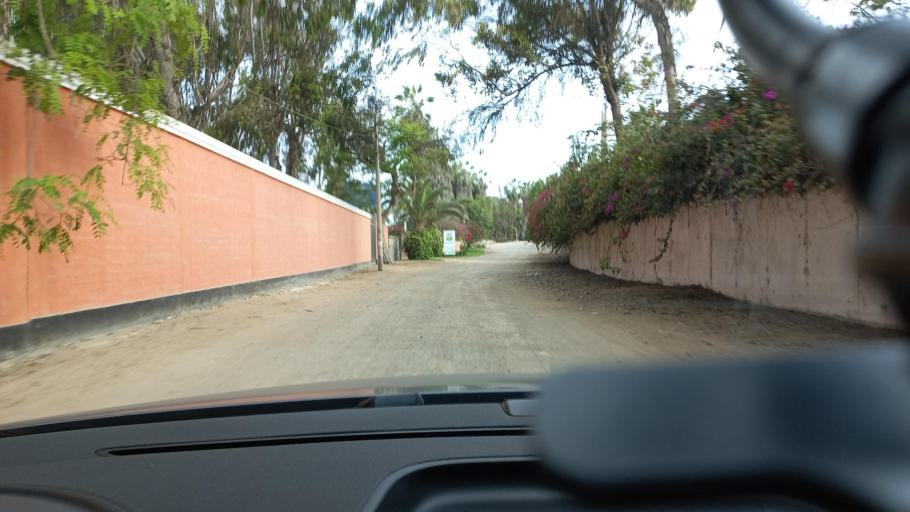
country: PE
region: Lima
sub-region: Lima
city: Punta Hermosa
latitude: -12.2625
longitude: -76.9076
